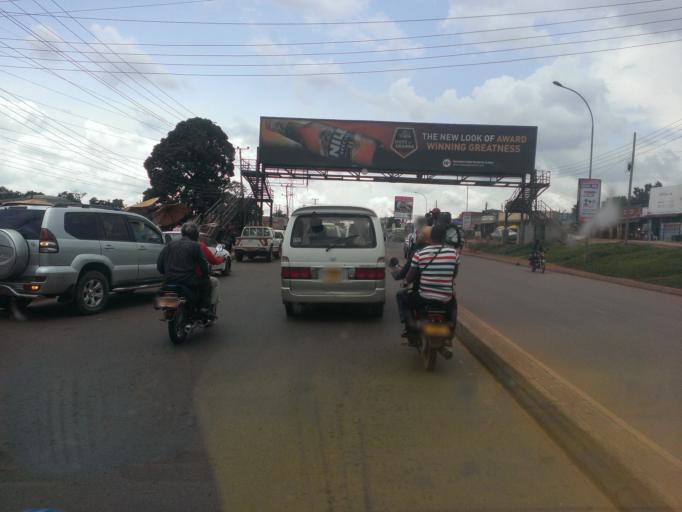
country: UG
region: Central Region
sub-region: Kampala District
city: Kampala
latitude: 0.3290
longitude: 32.6127
